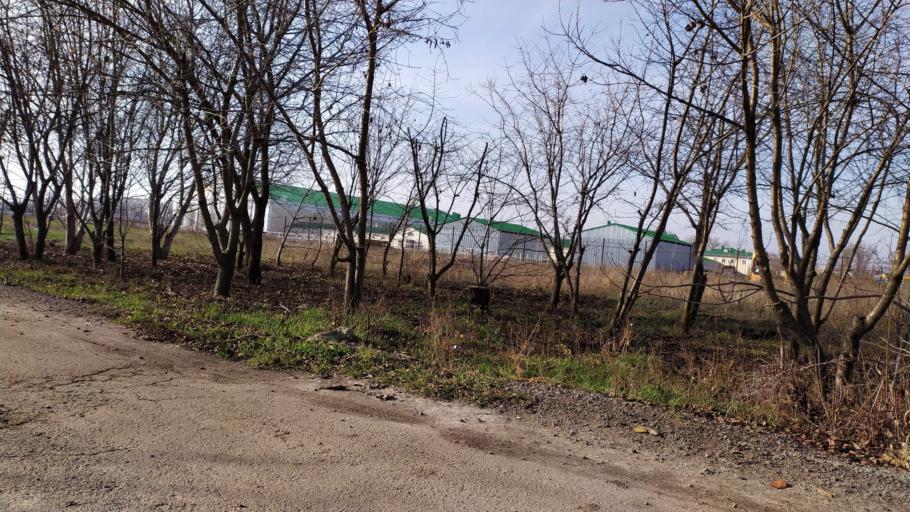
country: RU
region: Kursk
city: Kursk
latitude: 51.6428
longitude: 36.1317
